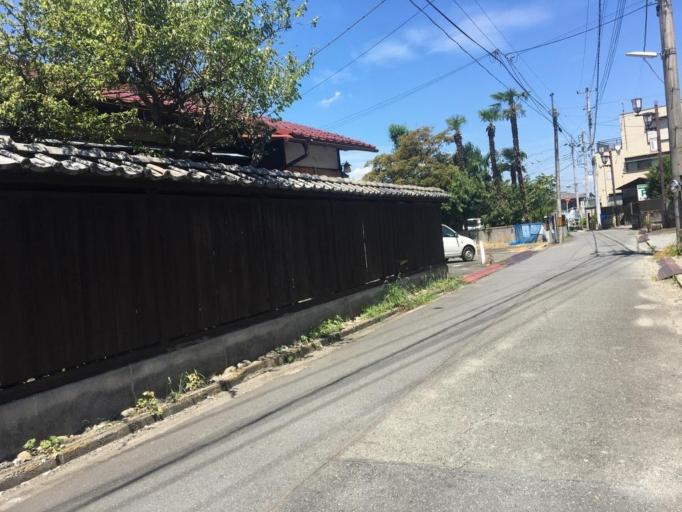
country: JP
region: Saitama
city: Chichibu
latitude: 35.9919
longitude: 139.0786
